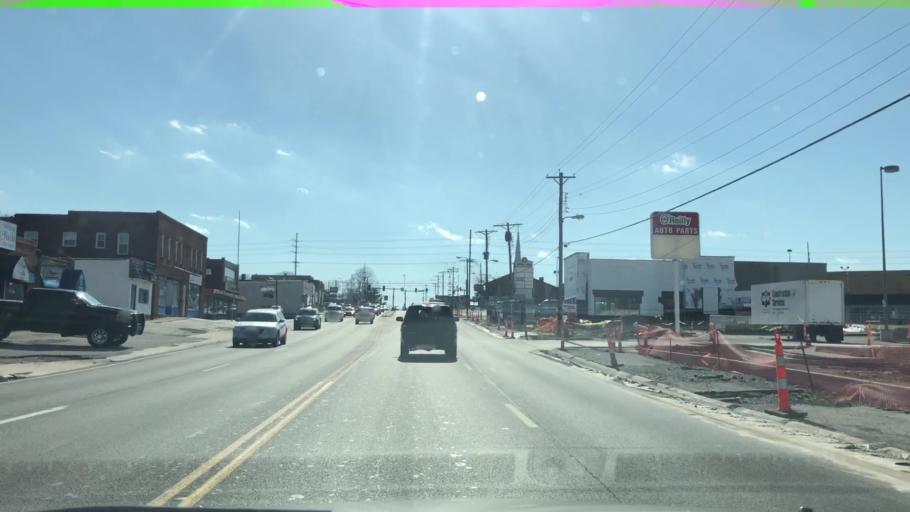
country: US
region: Missouri
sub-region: Saint Louis County
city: Affton
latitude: 38.5534
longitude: -90.3209
